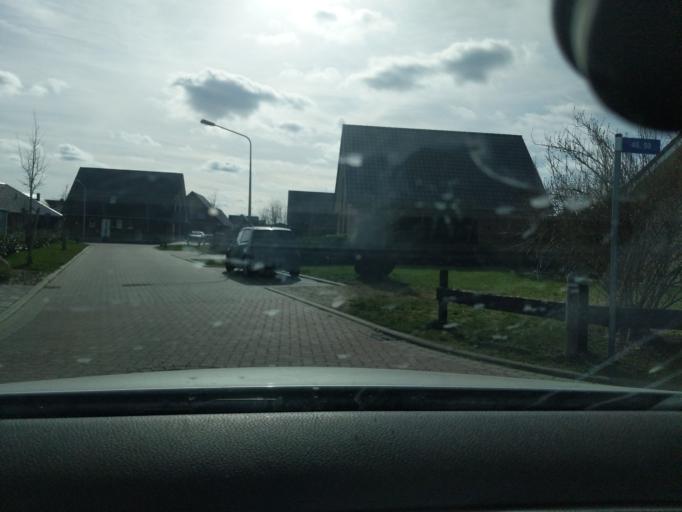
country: DE
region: Lower Saxony
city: Drochtersen
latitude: 53.6855
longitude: 9.4294
